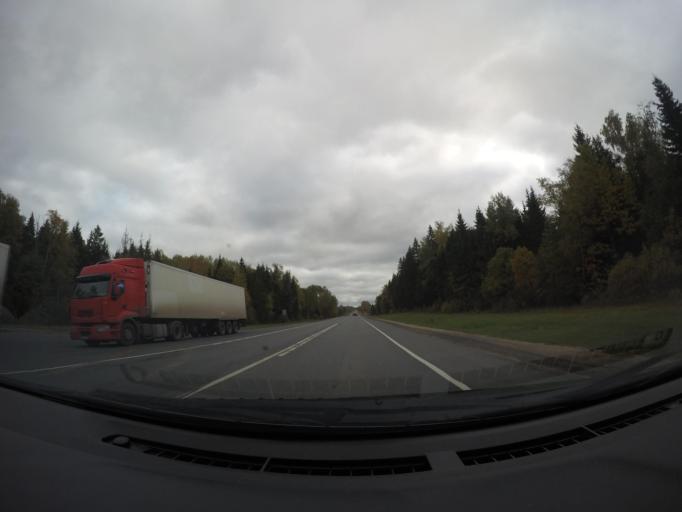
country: RU
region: Moskovskaya
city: Dorokhovo
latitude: 55.6021
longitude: 36.3578
